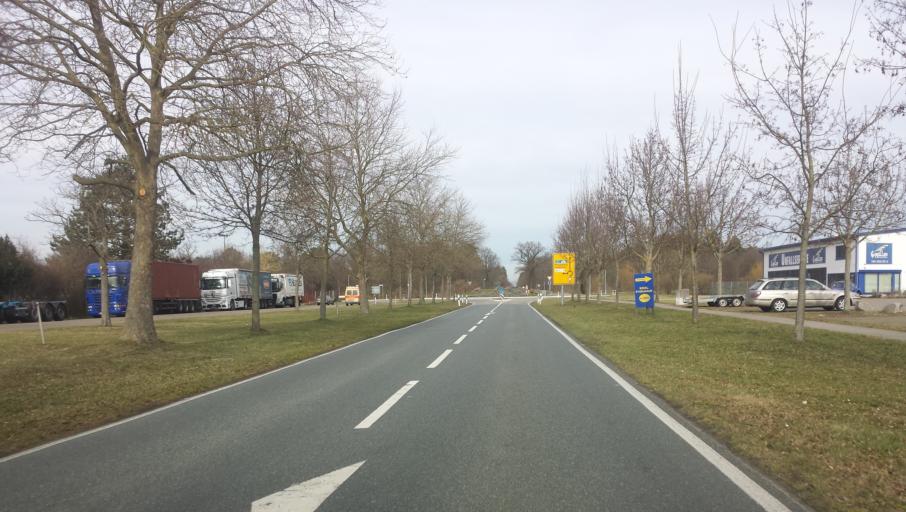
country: DE
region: Baden-Wuerttemberg
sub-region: Karlsruhe Region
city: Waghausel
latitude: 49.2516
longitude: 8.5454
